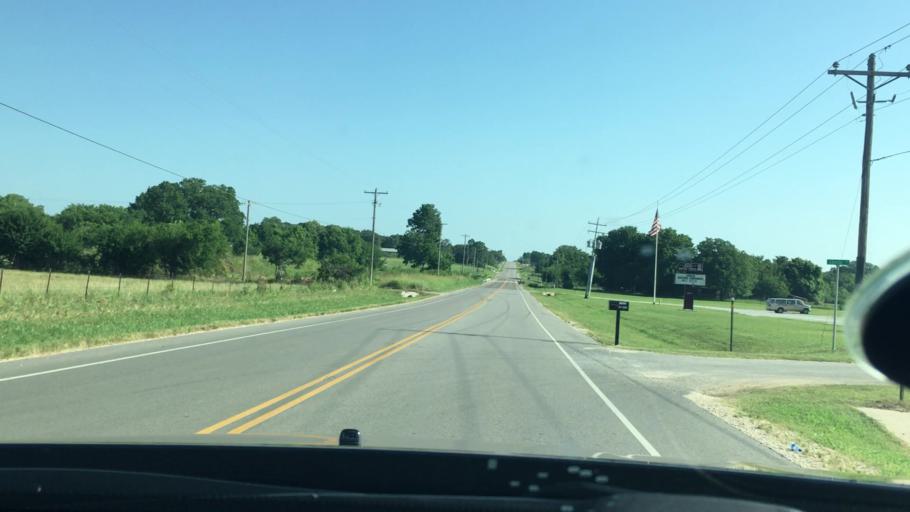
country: US
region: Oklahoma
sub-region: Pontotoc County
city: Ada
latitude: 34.7990
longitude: -96.6523
